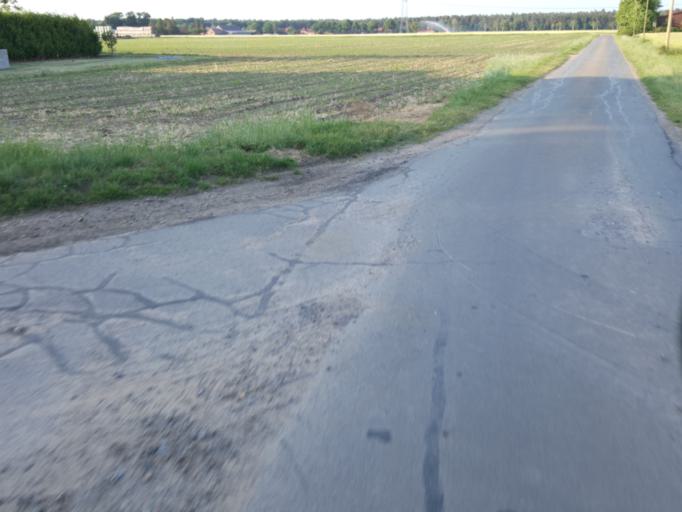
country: DE
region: Lower Saxony
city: Landesbergen
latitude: 52.5463
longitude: 9.1406
